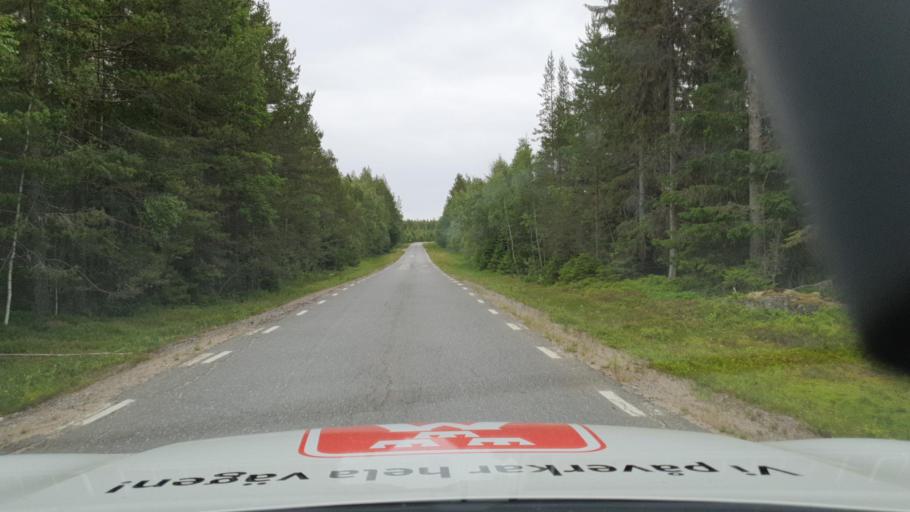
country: SE
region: Vaesterbotten
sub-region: Nordmalings Kommun
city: Nordmaling
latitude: 63.4332
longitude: 19.4772
